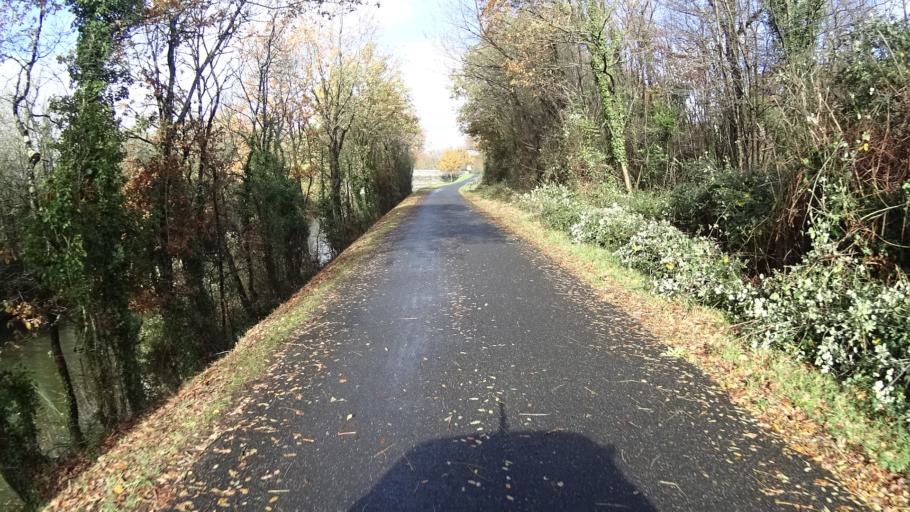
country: FR
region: Pays de la Loire
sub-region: Departement de la Loire-Atlantique
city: Saint-Nicolas-de-Redon
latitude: 47.6312
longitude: -2.0749
